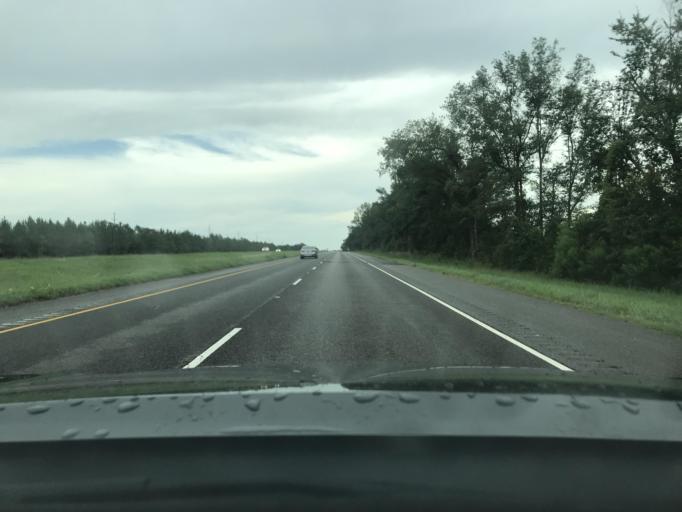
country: US
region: Louisiana
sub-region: Calcasieu Parish
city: Moss Bluff
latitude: 30.3920
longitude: -93.2243
